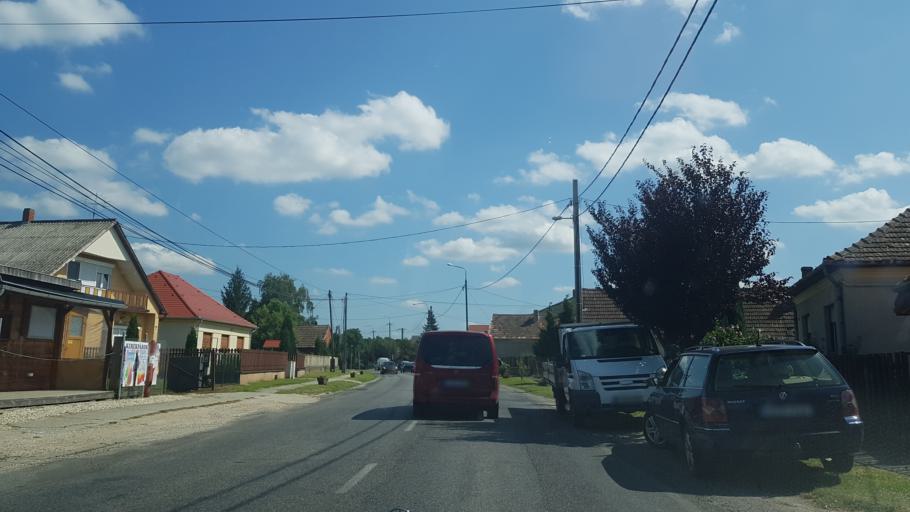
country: HU
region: Somogy
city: Marcali
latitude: 46.5223
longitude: 17.4191
